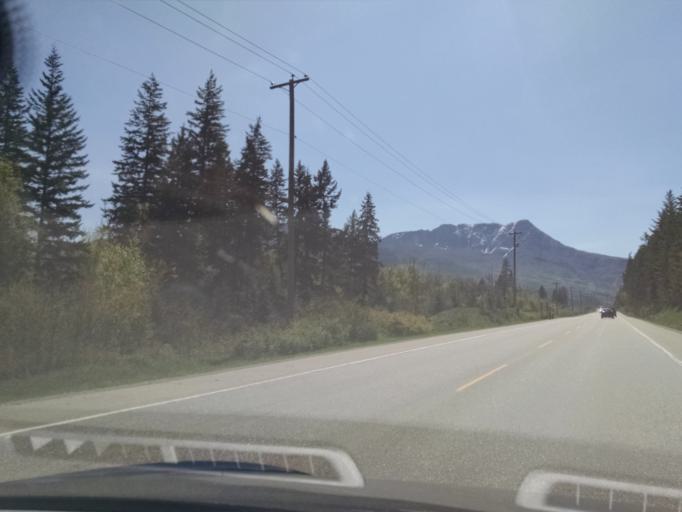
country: CA
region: British Columbia
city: Salmon Arm
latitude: 50.7210
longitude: -119.3174
